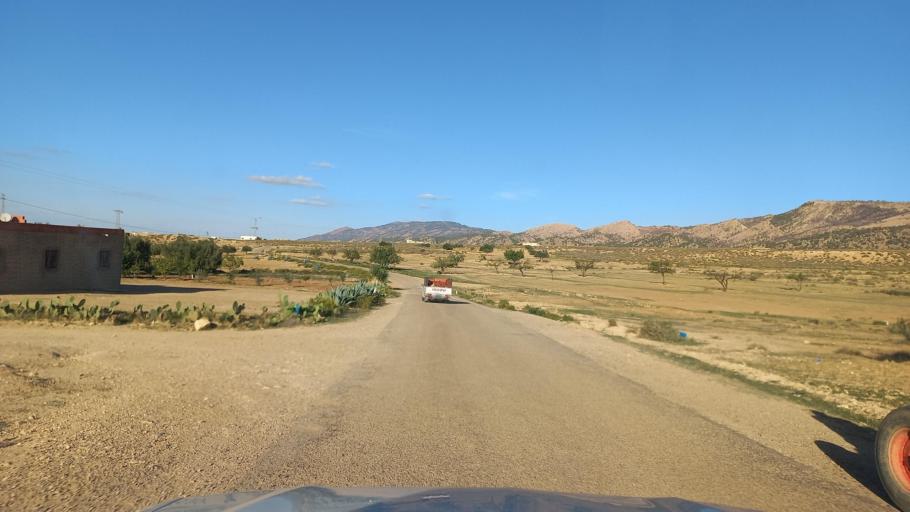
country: TN
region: Al Qasrayn
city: Sbiba
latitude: 35.3510
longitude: 9.1338
